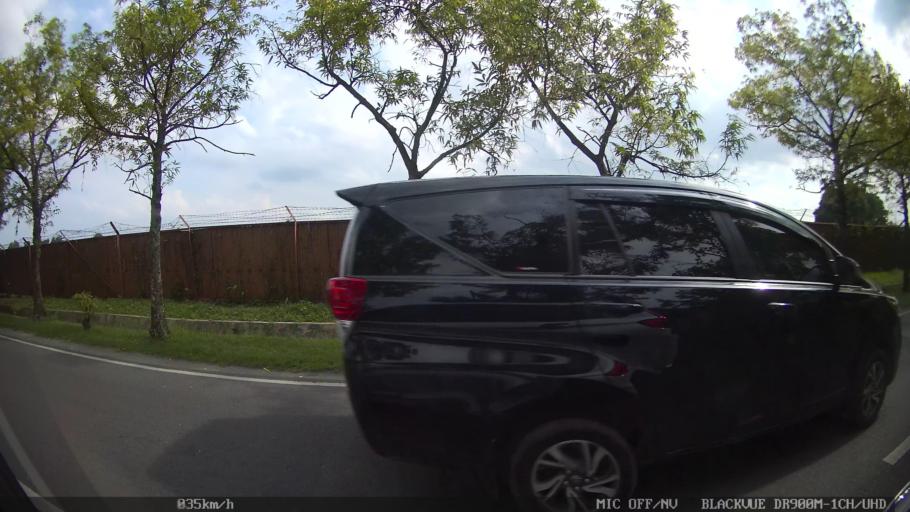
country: ID
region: North Sumatra
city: Medan
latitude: 3.5693
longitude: 98.6806
